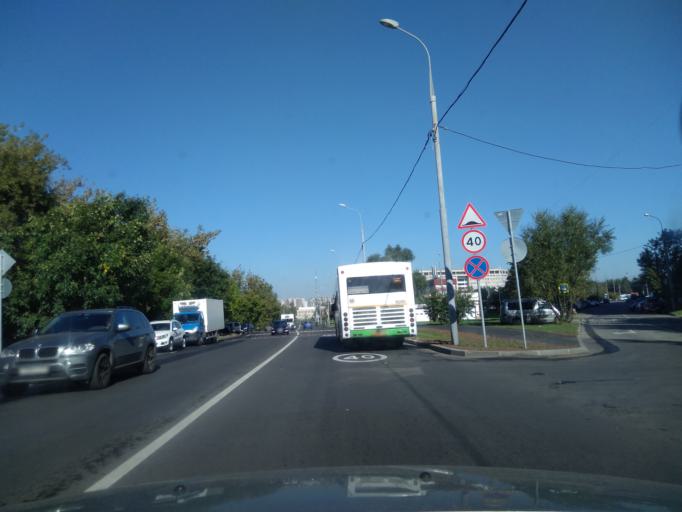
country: RU
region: Moscow
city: Strogino
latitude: 55.8478
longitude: 37.4036
